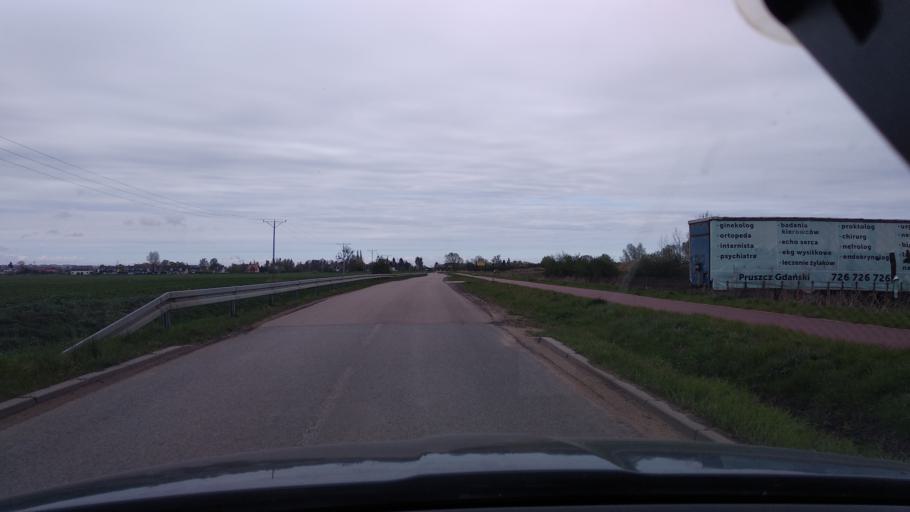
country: PL
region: Pomeranian Voivodeship
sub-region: Powiat gdanski
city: Pruszcz Gdanski
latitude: 54.2706
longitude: 18.6599
